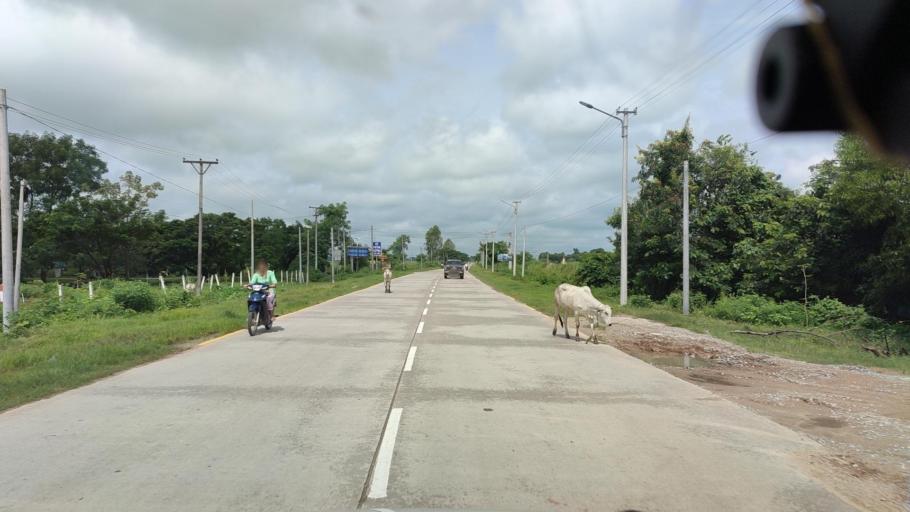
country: MM
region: Bago
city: Taungoo
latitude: 18.9533
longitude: 96.4203
